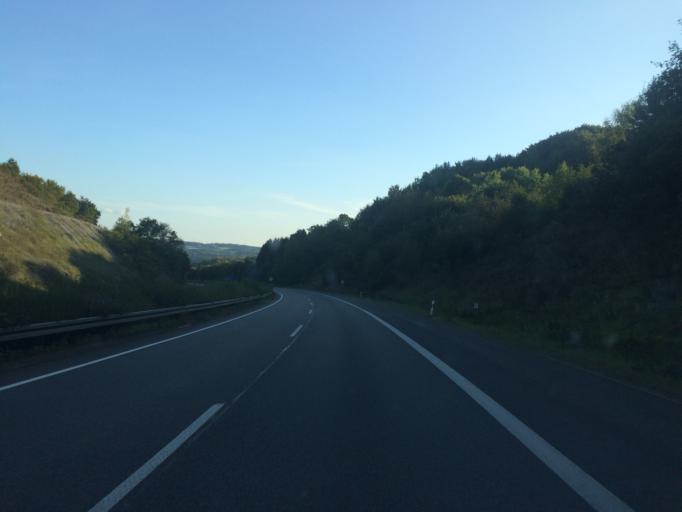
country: DE
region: Saarland
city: Tholey
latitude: 49.4714
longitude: 6.9737
